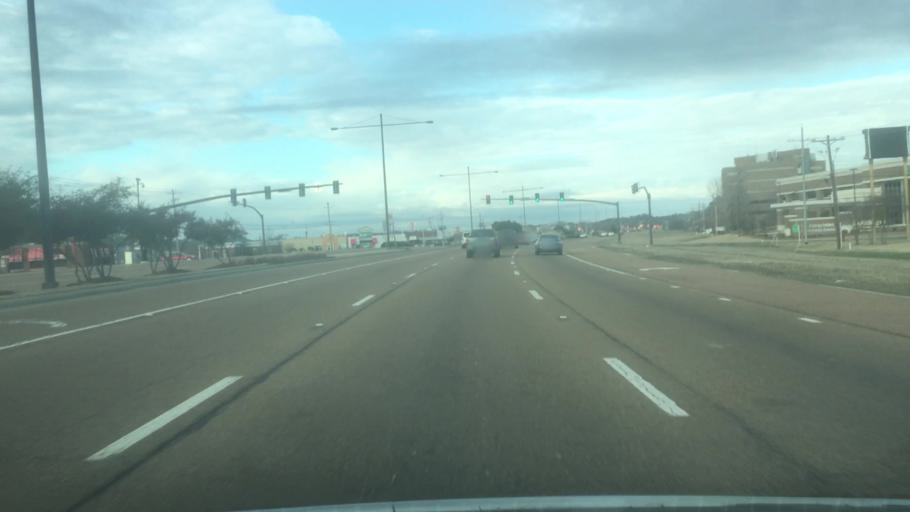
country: US
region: Mississippi
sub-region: Rankin County
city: Flowood
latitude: 32.3291
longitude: -90.1182
